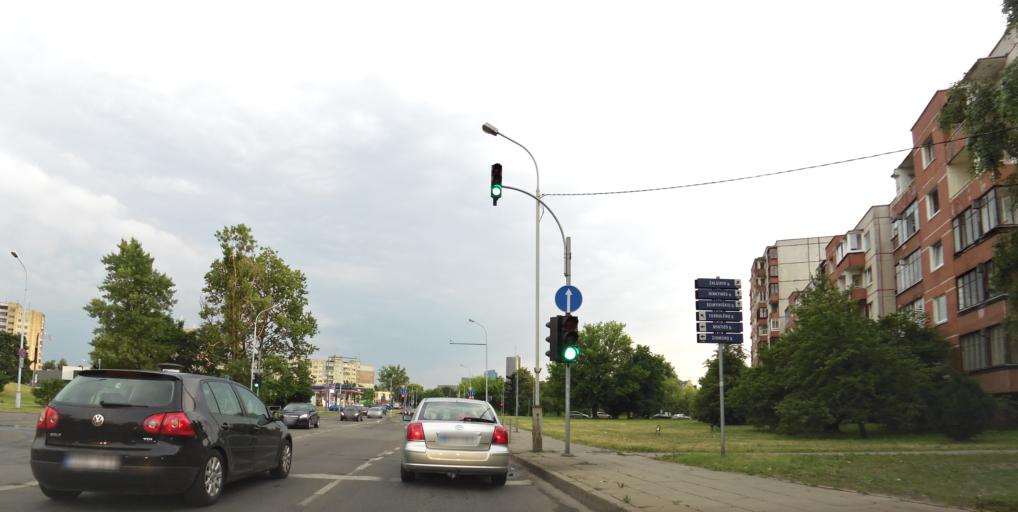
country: LT
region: Vilnius County
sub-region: Vilnius
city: Vilnius
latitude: 54.7044
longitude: 25.2890
